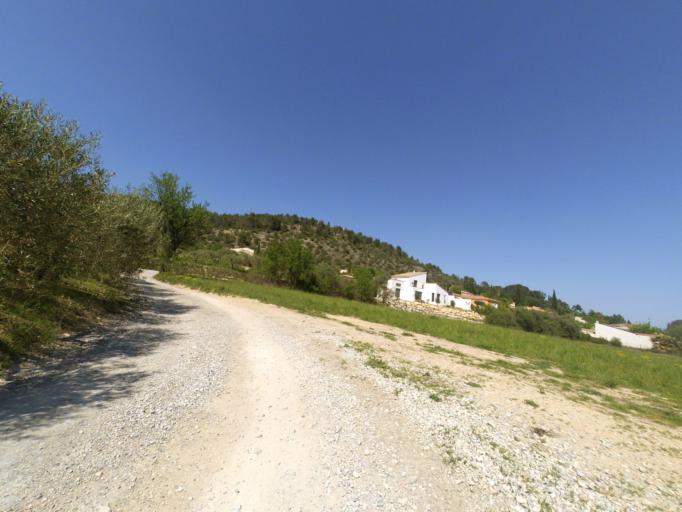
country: FR
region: Languedoc-Roussillon
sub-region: Departement du Gard
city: Calvisson
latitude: 43.7783
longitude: 4.1827
